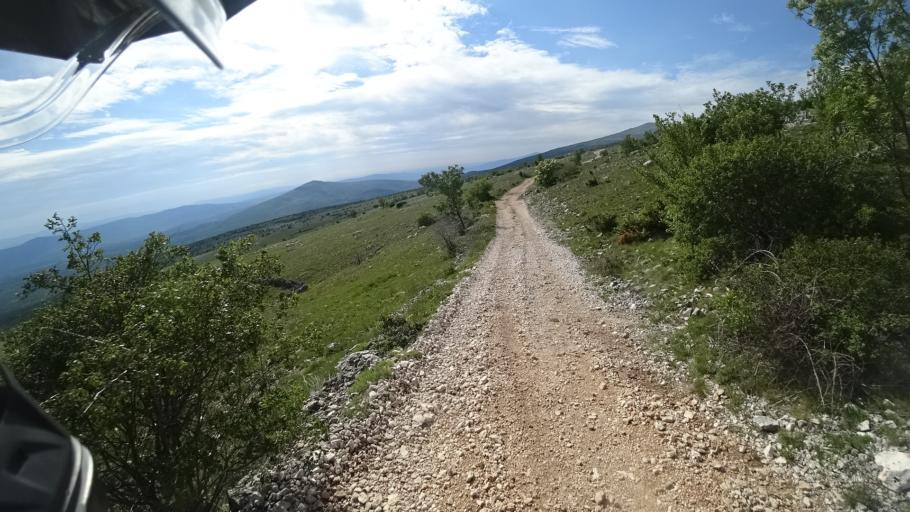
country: HR
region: Splitsko-Dalmatinska
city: Hrvace
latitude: 43.7755
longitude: 16.4549
